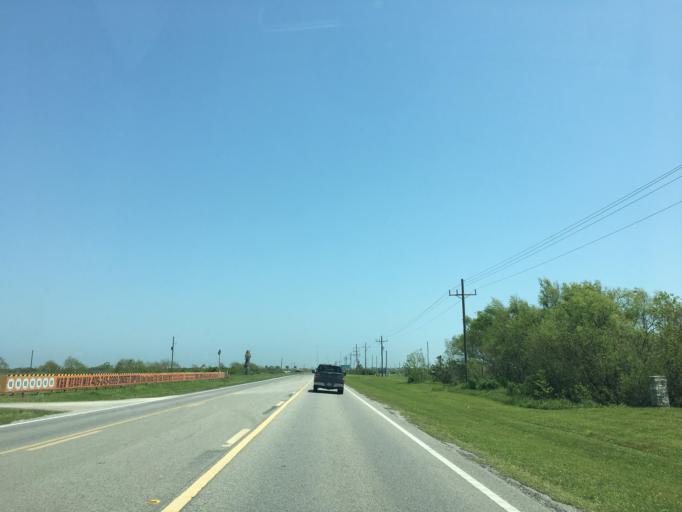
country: US
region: Texas
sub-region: Galveston County
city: Bolivar Peninsula
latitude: 29.4333
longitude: -94.6816
